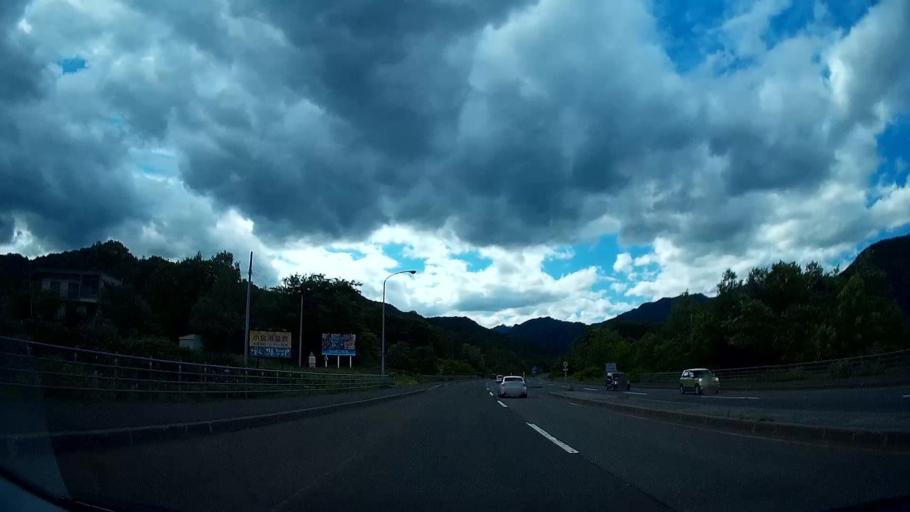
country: JP
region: Hokkaido
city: Sapporo
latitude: 42.9579
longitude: 141.2296
